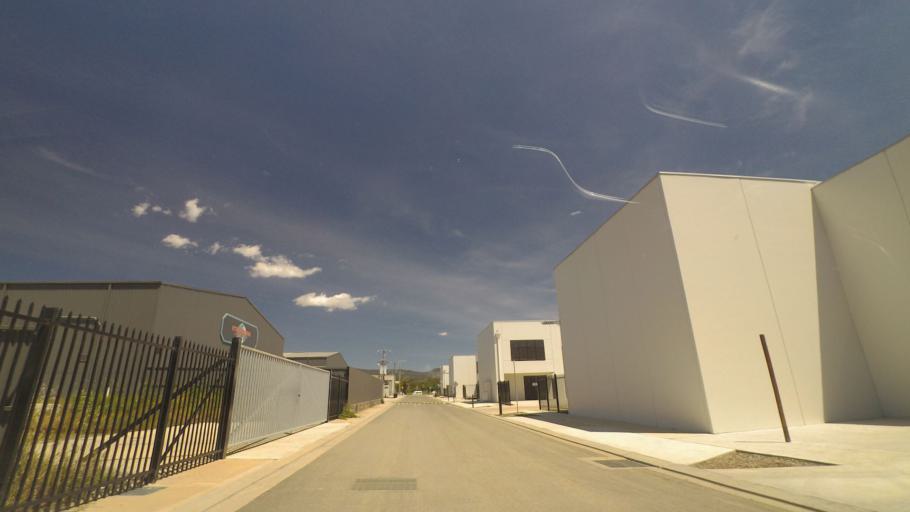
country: AU
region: Victoria
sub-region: Maroondah
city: Kilsyth South
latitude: -37.8150
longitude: 145.3203
